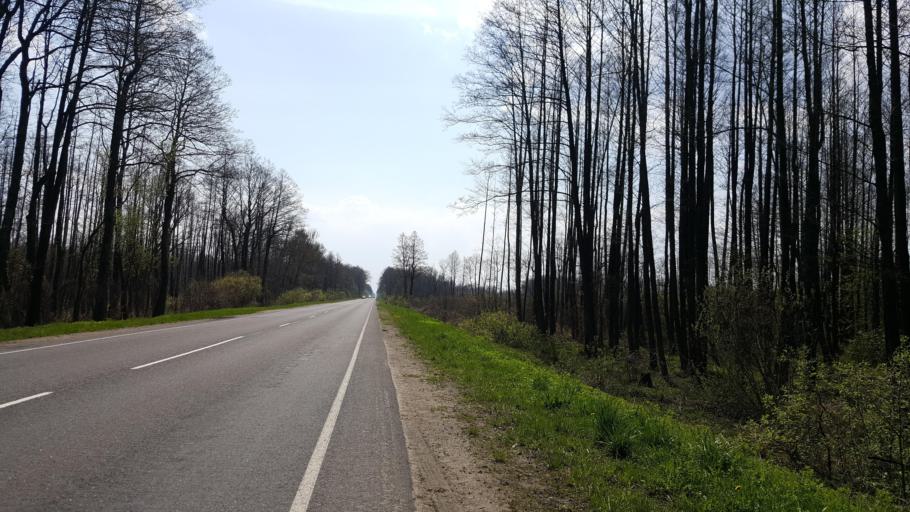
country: BY
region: Brest
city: Zhabinka
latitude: 52.2828
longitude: 23.9467
